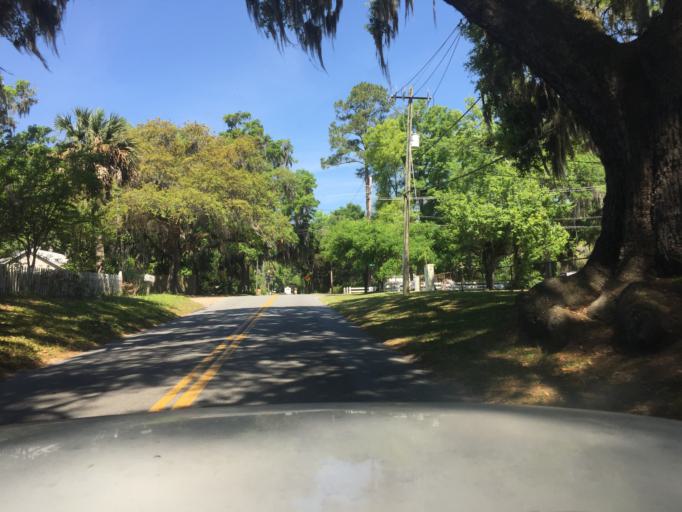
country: US
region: Georgia
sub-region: Chatham County
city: Montgomery
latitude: 31.9437
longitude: -81.1098
